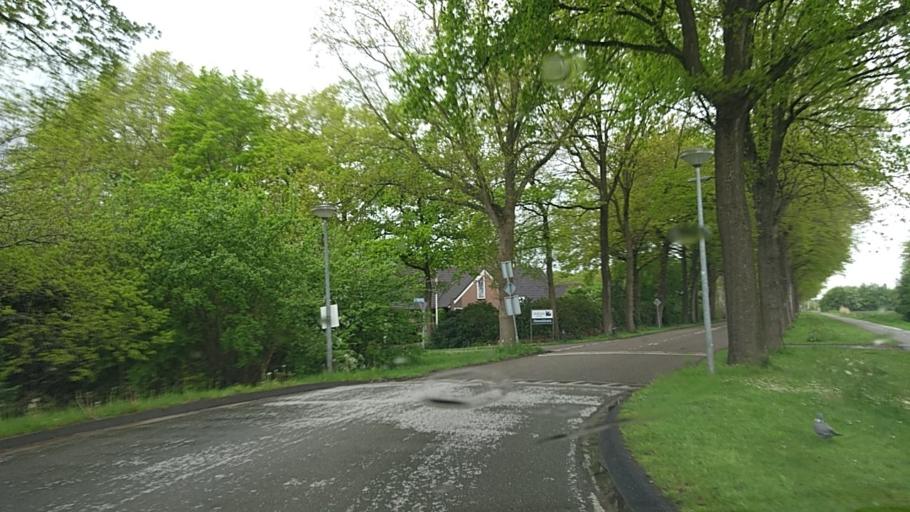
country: NL
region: Drenthe
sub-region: Gemeente Westerveld
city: Havelte
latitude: 52.7794
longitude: 6.2339
